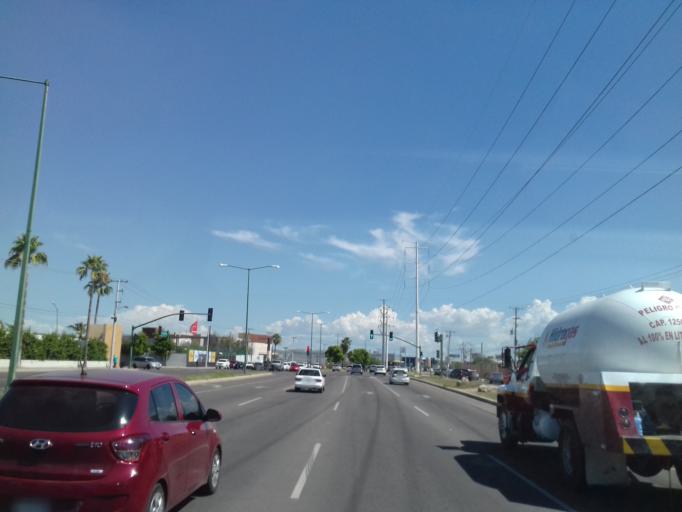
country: MX
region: Sonora
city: Hermosillo
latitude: 29.0845
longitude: -110.9976
